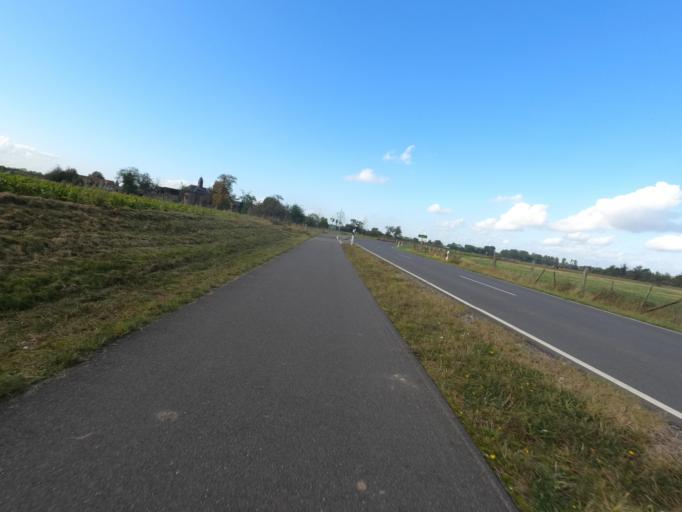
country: DE
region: North Rhine-Westphalia
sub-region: Regierungsbezirk Koln
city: Inden
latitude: 50.8871
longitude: 6.3802
